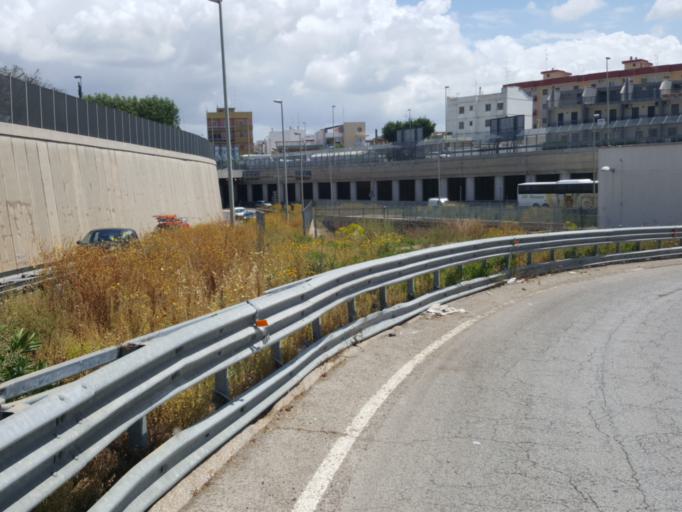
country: IT
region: Apulia
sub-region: Provincia di Bari
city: Modugno
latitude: 41.0875
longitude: 16.7750
